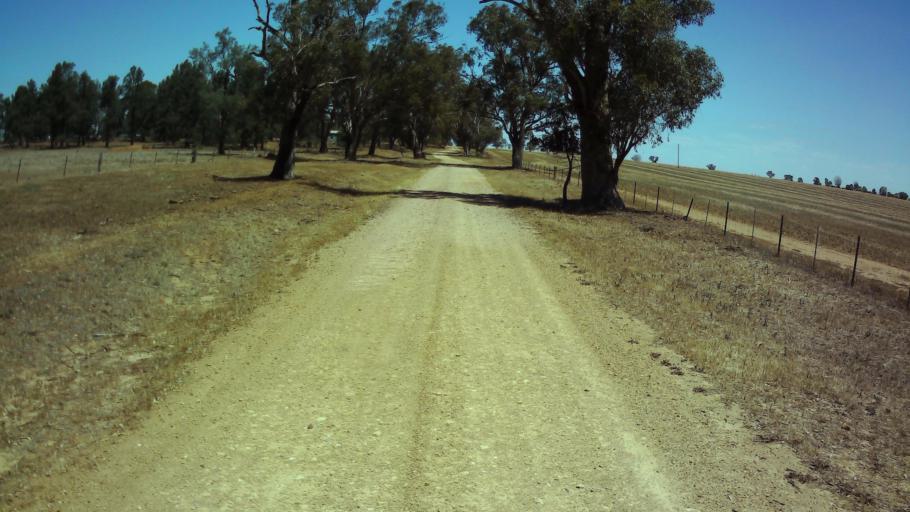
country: AU
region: New South Wales
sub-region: Weddin
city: Grenfell
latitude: -34.0131
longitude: 148.3523
